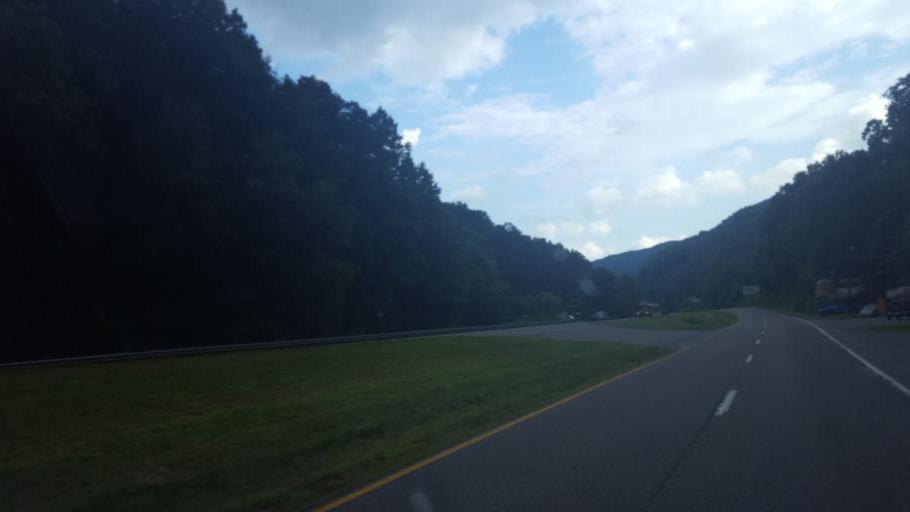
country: US
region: Virginia
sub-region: Wise County
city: Wise
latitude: 37.0477
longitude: -82.6000
